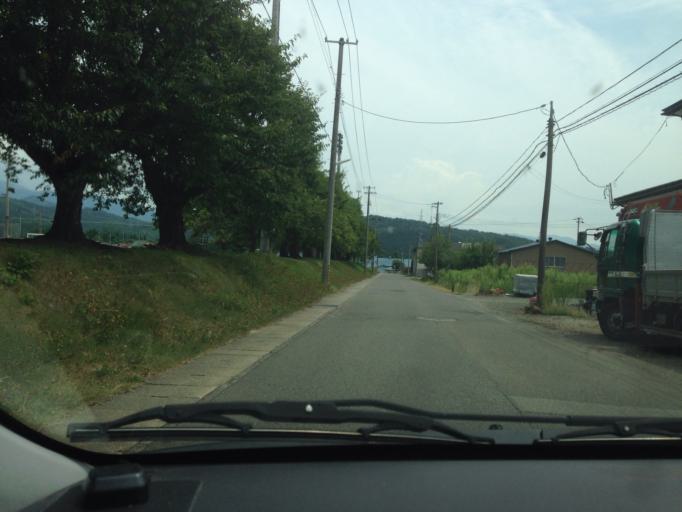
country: JP
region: Fukushima
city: Kitakata
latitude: 37.7181
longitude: 139.8723
